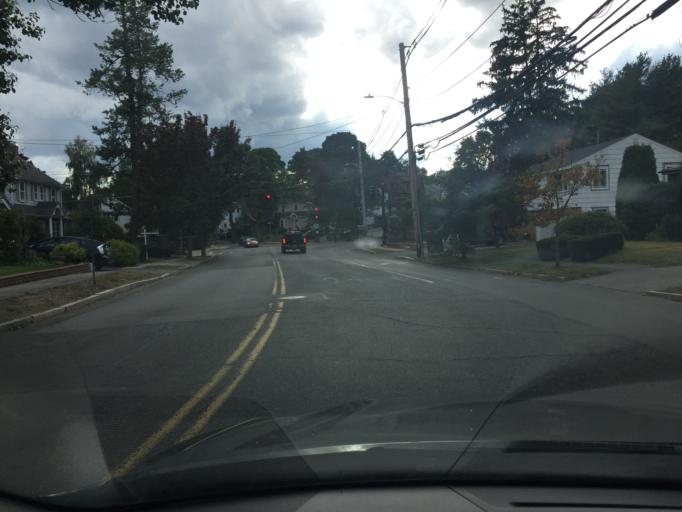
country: US
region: Massachusetts
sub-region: Middlesex County
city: Medford
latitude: 42.4244
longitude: -71.1204
